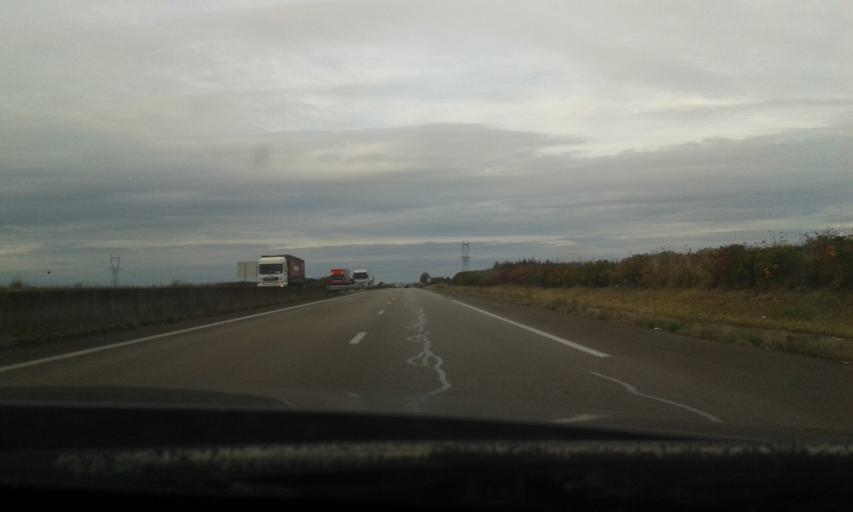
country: FR
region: Haute-Normandie
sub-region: Departement de l'Eure
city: La Madeleine-de-Nonancourt
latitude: 48.8457
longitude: 1.1811
